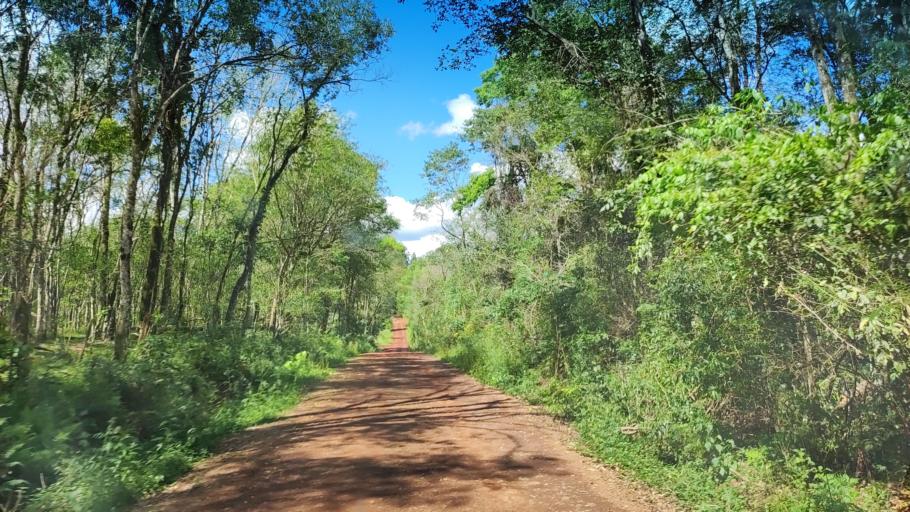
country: AR
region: Misiones
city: Ruiz de Montoya
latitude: -26.9529
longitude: -55.0283
